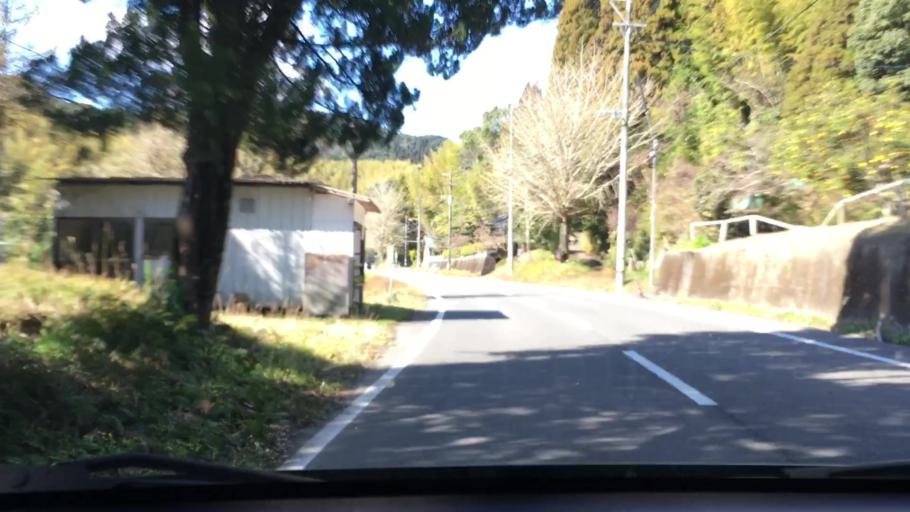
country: JP
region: Kagoshima
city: Ijuin
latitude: 31.7068
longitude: 130.4443
